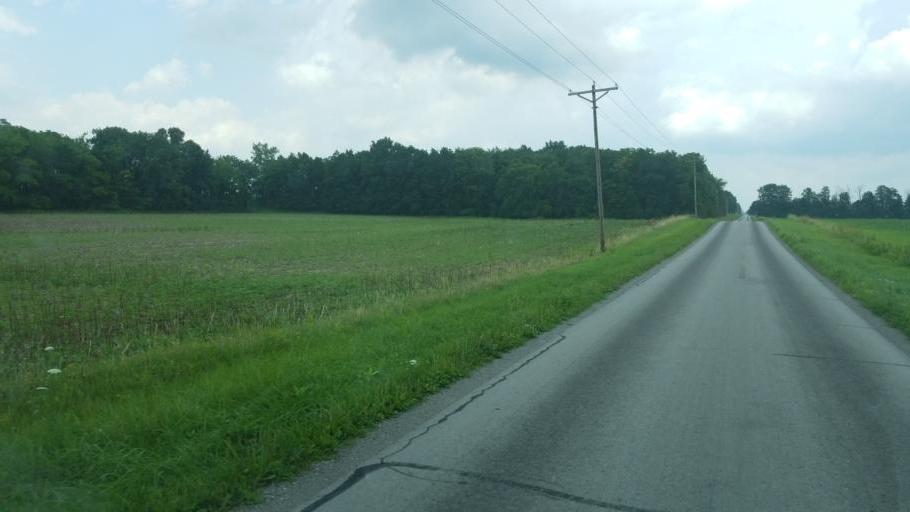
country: US
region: Ohio
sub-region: Hardin County
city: Kenton
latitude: 40.5789
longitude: -83.5730
